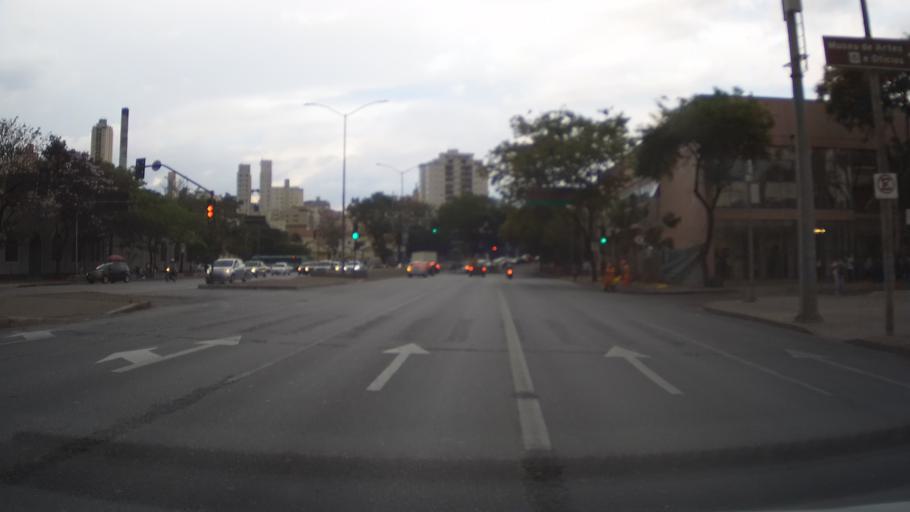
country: BR
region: Minas Gerais
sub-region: Belo Horizonte
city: Belo Horizonte
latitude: -19.9164
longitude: -43.9340
